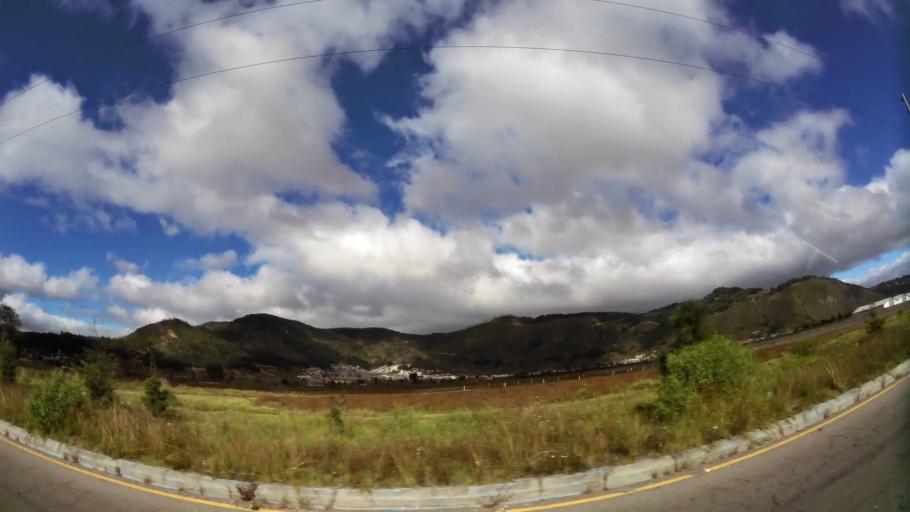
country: GT
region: Quetzaltenango
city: Salcaja
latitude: 14.8920
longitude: -91.4642
